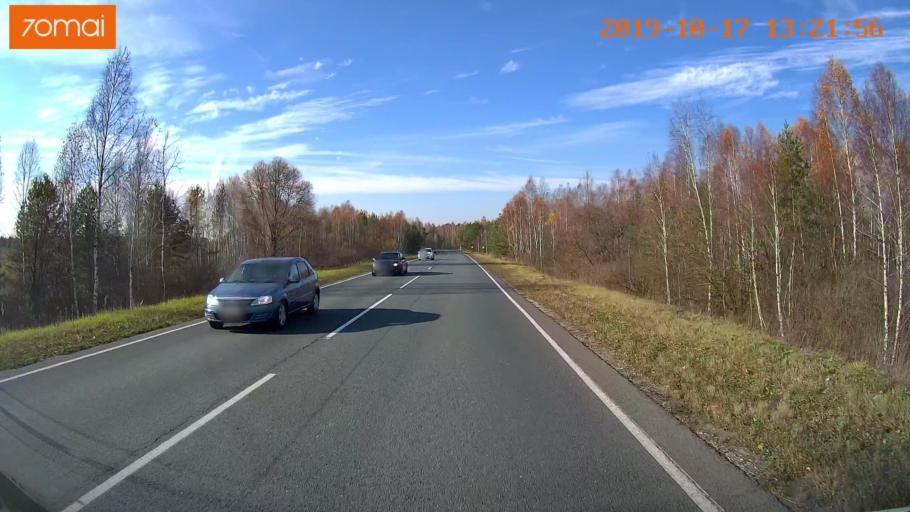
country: RU
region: Rjazan
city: Gus'-Zheleznyy
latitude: 55.0838
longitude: 41.0151
